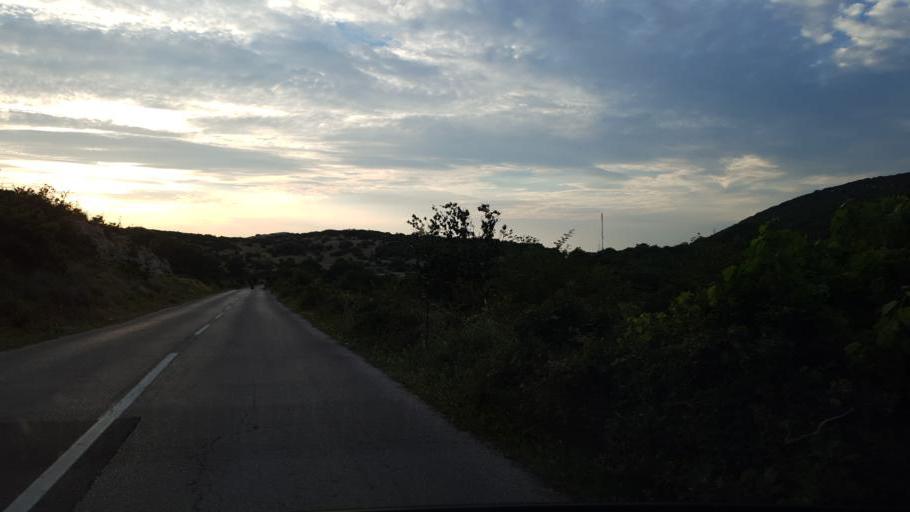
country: HR
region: Primorsko-Goranska
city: Punat
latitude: 44.9839
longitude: 14.6514
